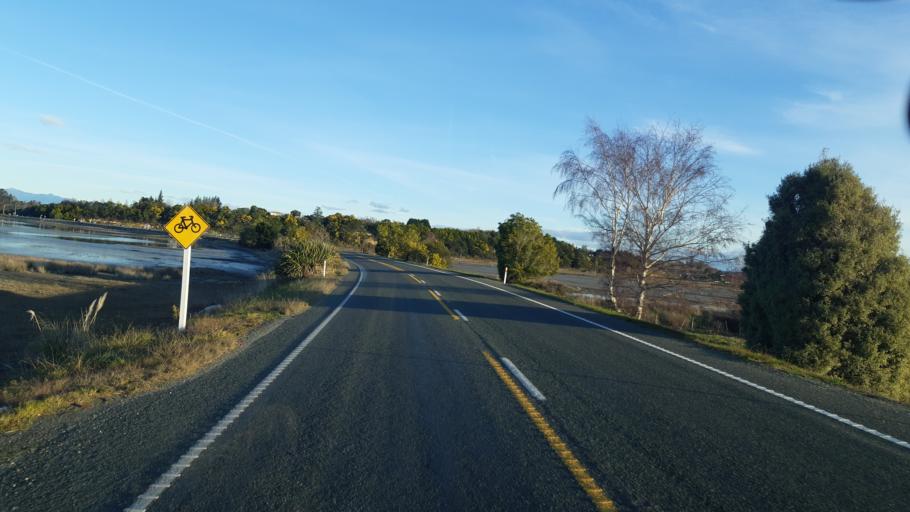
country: NZ
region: Tasman
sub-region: Tasman District
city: Motueka
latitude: -41.1399
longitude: 173.0085
